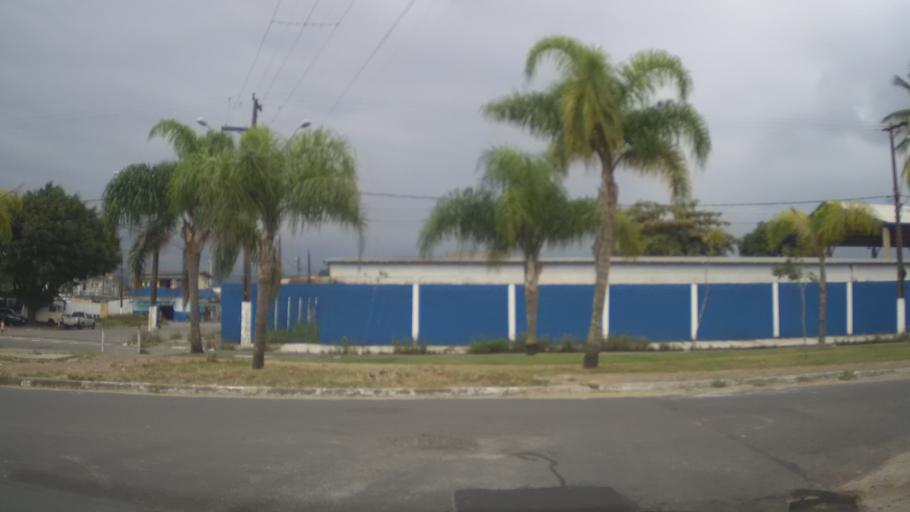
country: BR
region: Sao Paulo
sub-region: Praia Grande
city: Praia Grande
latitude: -24.0043
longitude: -46.4483
